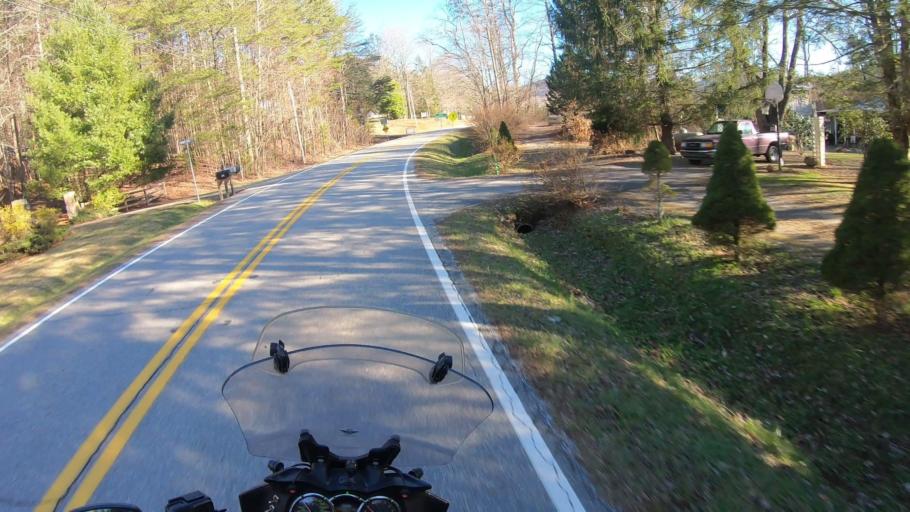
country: US
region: Georgia
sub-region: Lumpkin County
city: Dahlonega
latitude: 34.7057
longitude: -84.0384
